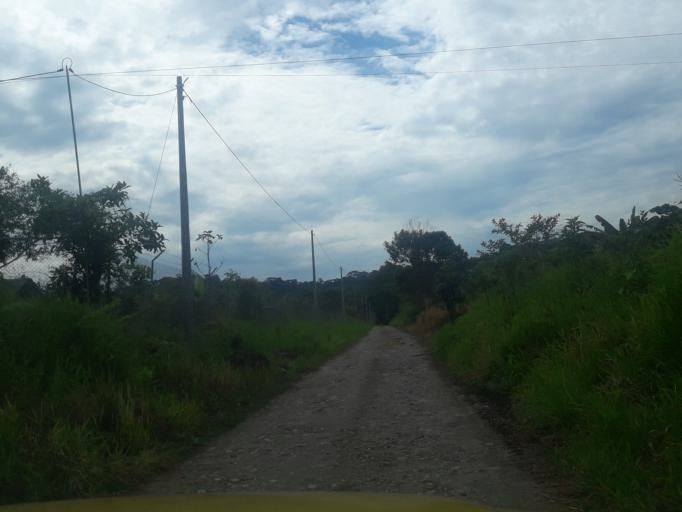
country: EC
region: Napo
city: Tena
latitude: -1.0575
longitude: -77.7966
